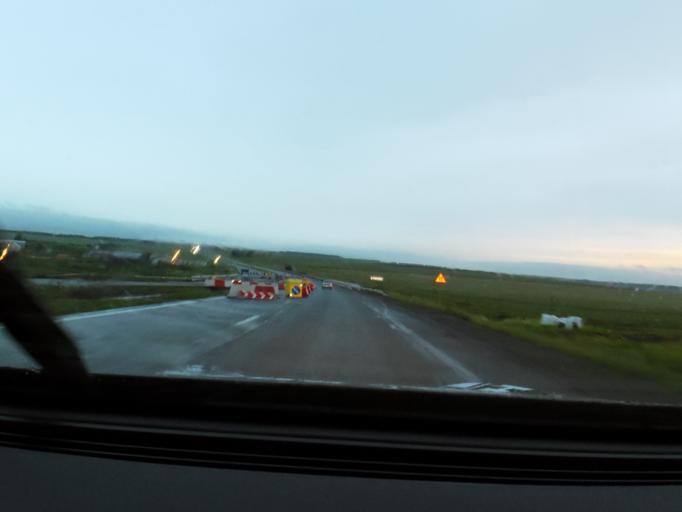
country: RU
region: Tatarstan
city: Yelabuga
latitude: 55.8093
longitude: 51.9613
